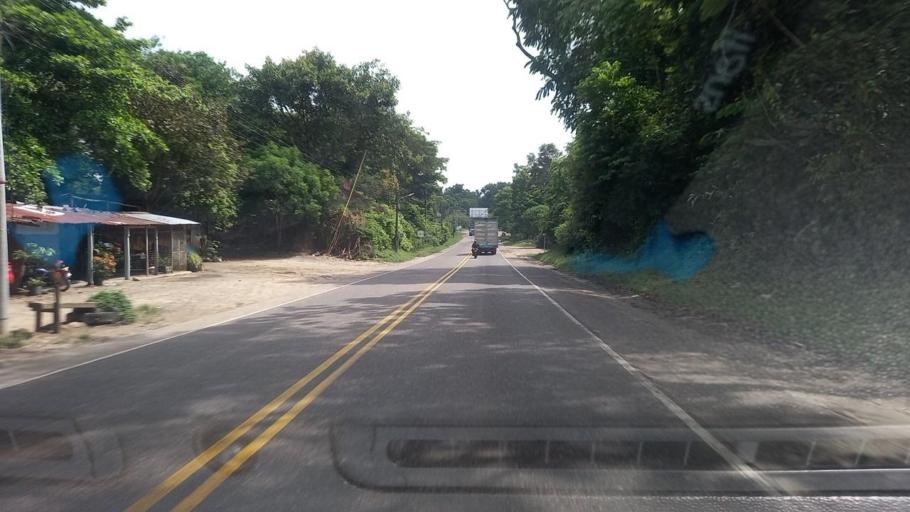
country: CO
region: Santander
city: Sabana de Torres
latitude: 7.1265
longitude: -73.5769
